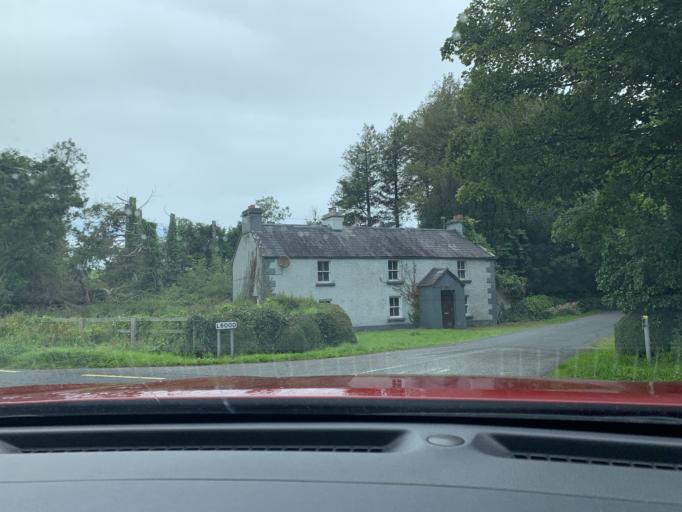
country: IE
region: Connaught
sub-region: County Leitrim
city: Carrick-on-Shannon
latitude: 53.8703
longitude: -8.1556
